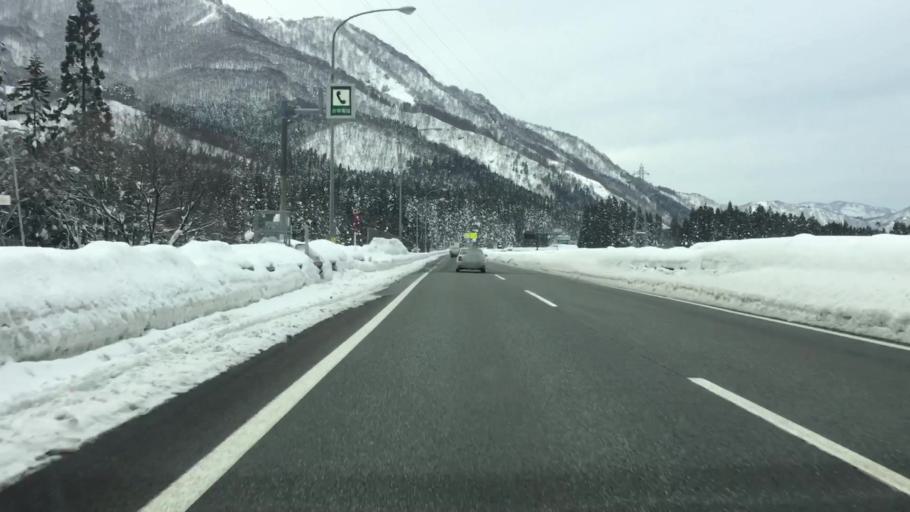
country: JP
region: Niigata
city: Shiozawa
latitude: 36.8793
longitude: 138.8565
